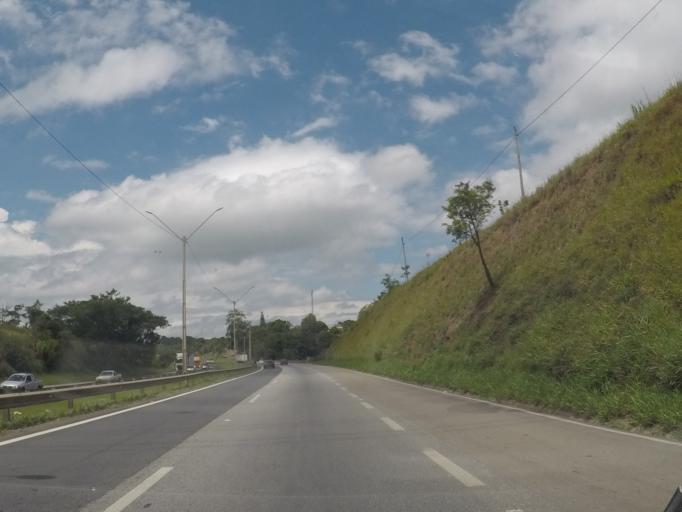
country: BR
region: Sao Paulo
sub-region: Atibaia
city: Atibaia
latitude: -23.0346
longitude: -46.5454
